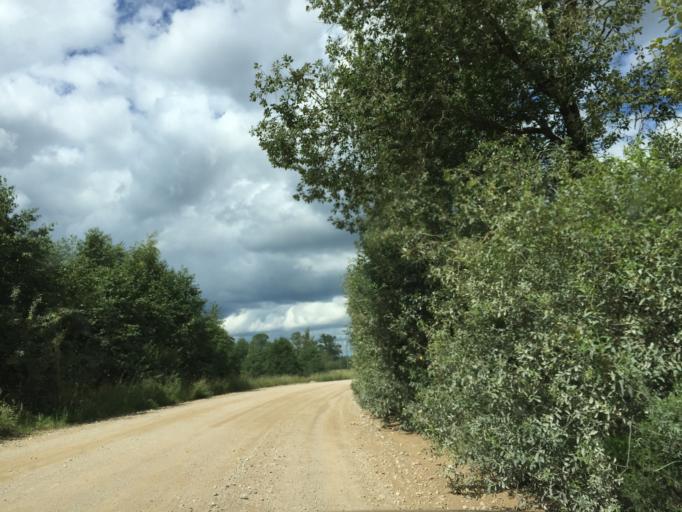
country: LV
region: Ropazu
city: Ropazi
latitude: 56.9061
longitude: 24.7797
